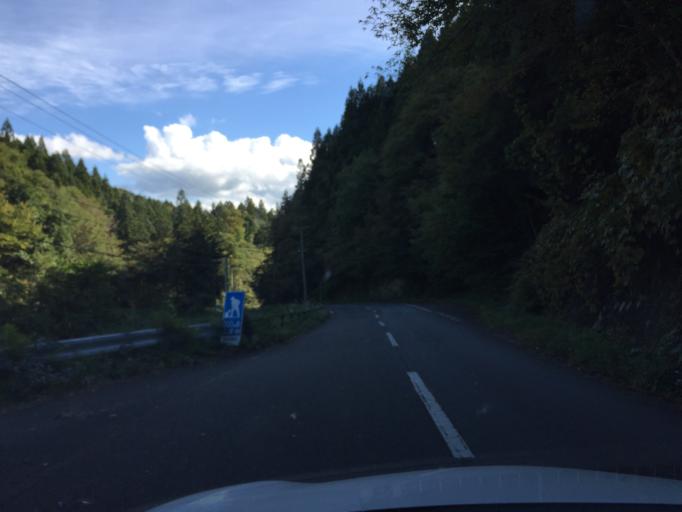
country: JP
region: Fukushima
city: Ishikawa
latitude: 37.1446
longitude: 140.5990
